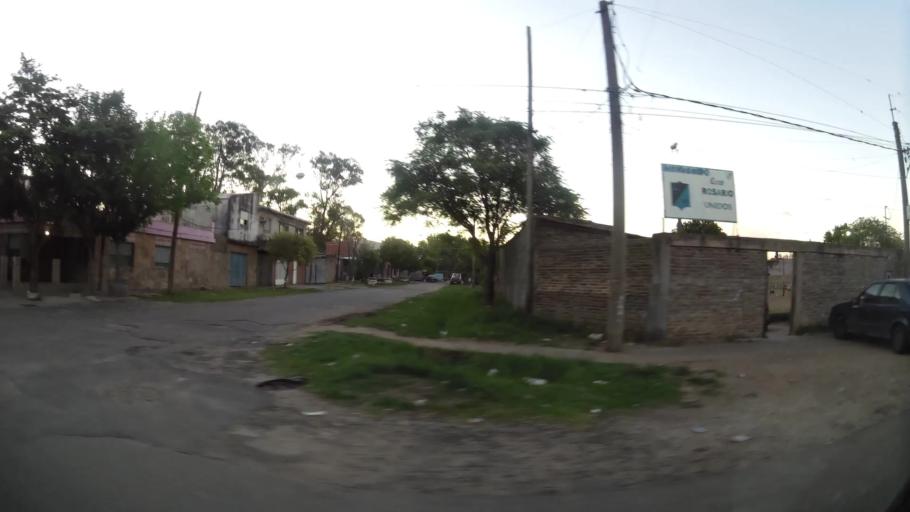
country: AR
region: Santa Fe
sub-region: Departamento de Rosario
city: Rosario
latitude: -32.9611
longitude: -60.6861
